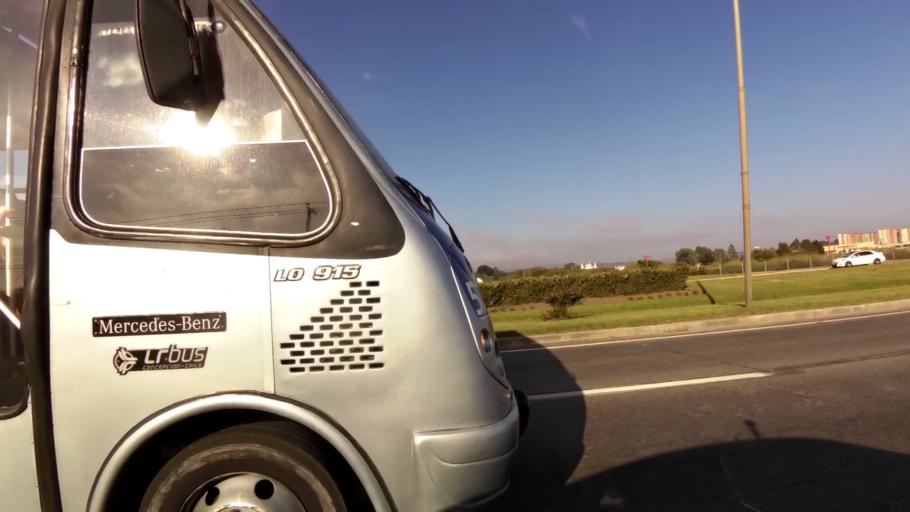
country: CL
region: Biobio
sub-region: Provincia de Concepcion
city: Concepcion
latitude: -36.7877
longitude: -73.0729
